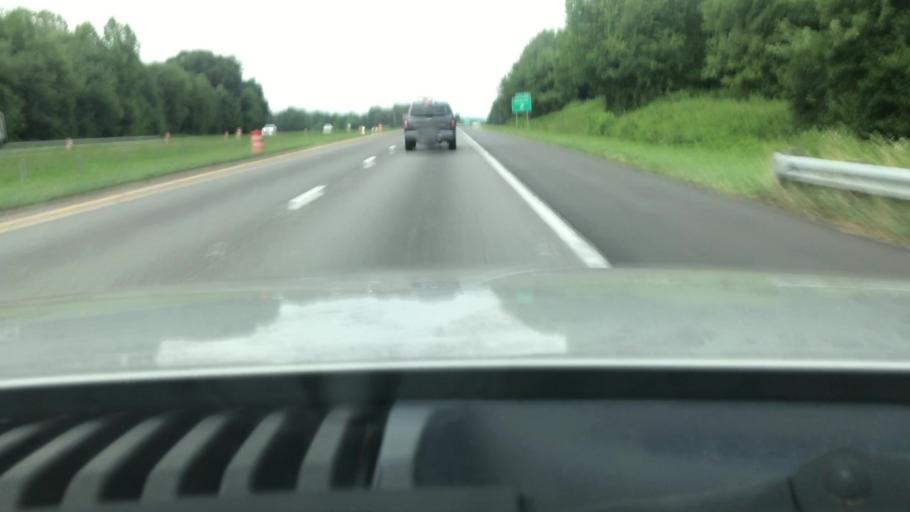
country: US
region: North Carolina
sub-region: Surry County
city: Dobson
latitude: 36.3881
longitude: -80.7884
